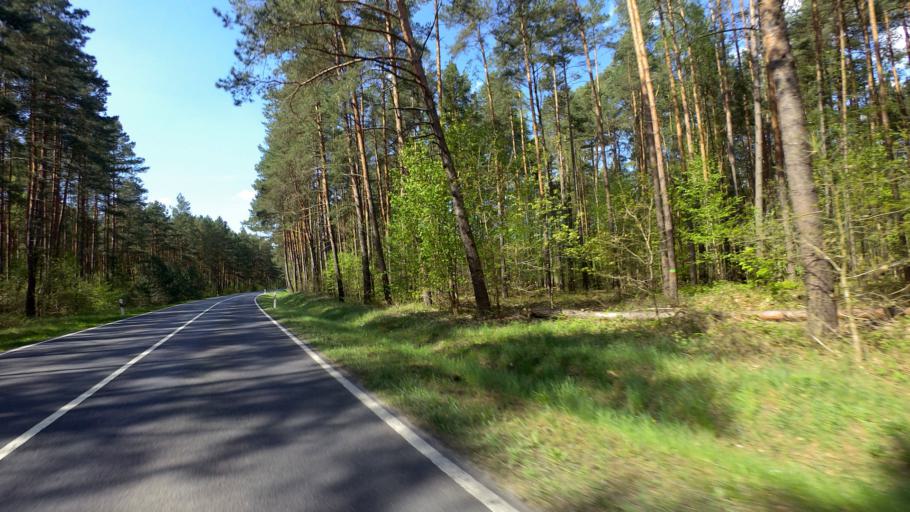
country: DE
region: Brandenburg
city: Templin
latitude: 53.1208
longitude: 13.5440
